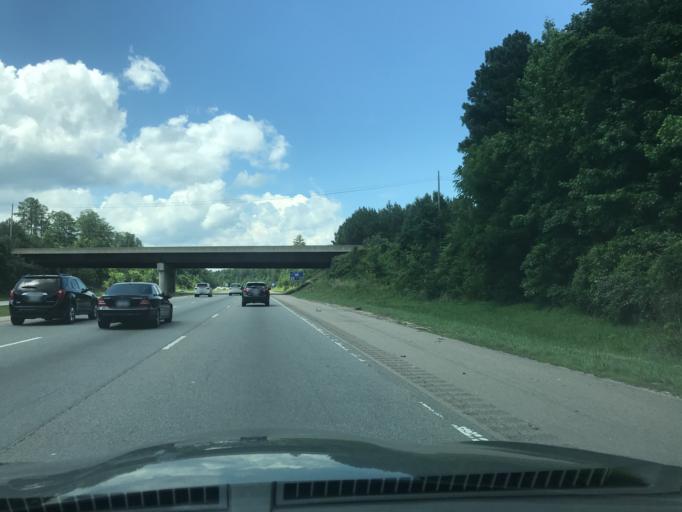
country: US
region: North Carolina
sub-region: Wake County
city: Raleigh
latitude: 35.8828
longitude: -78.5901
